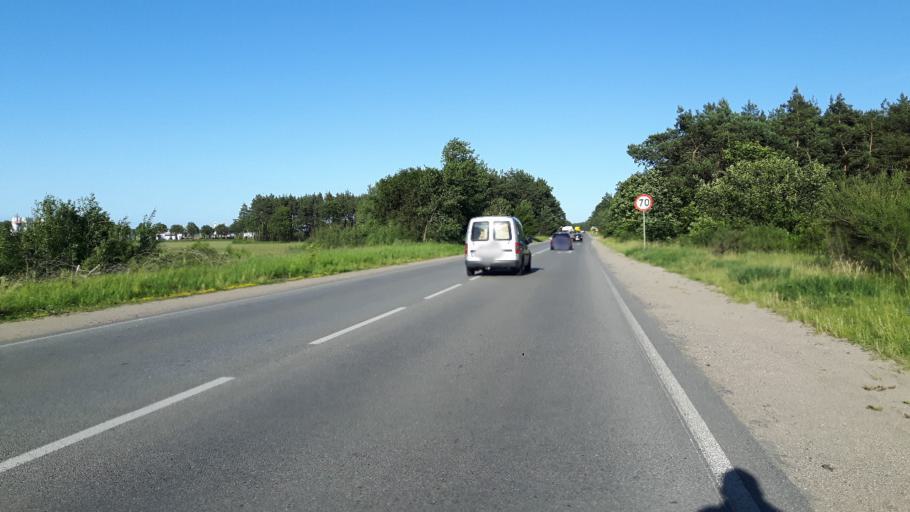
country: PL
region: Pomeranian Voivodeship
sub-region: Powiat pucki
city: Kosakowo
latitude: 54.6049
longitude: 18.4473
